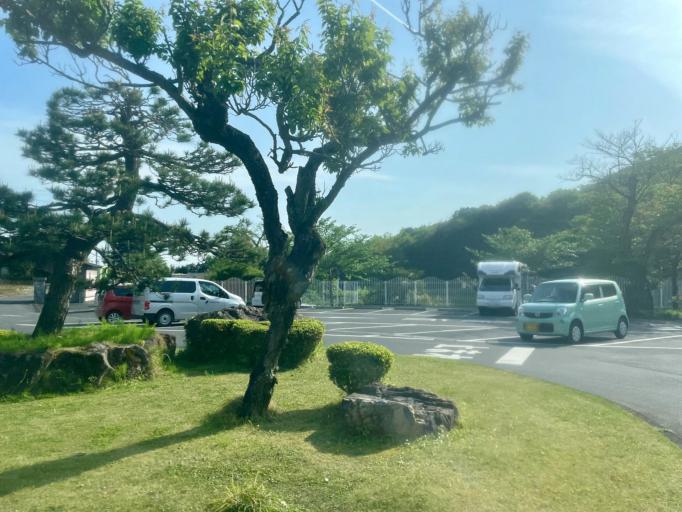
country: JP
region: Tochigi
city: Ashikaga
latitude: 36.3366
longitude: 139.5049
